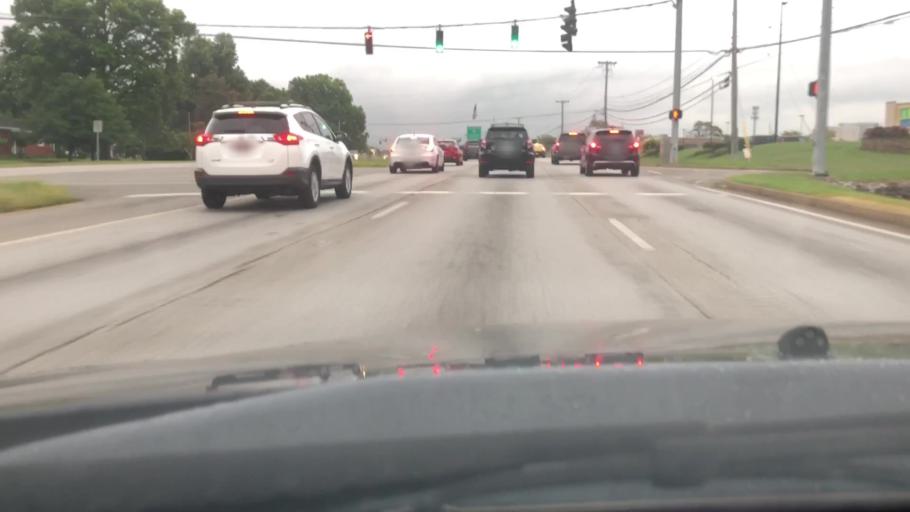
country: US
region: Kentucky
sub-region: Jefferson County
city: Hurstbourne Acres
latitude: 38.2172
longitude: -85.5871
